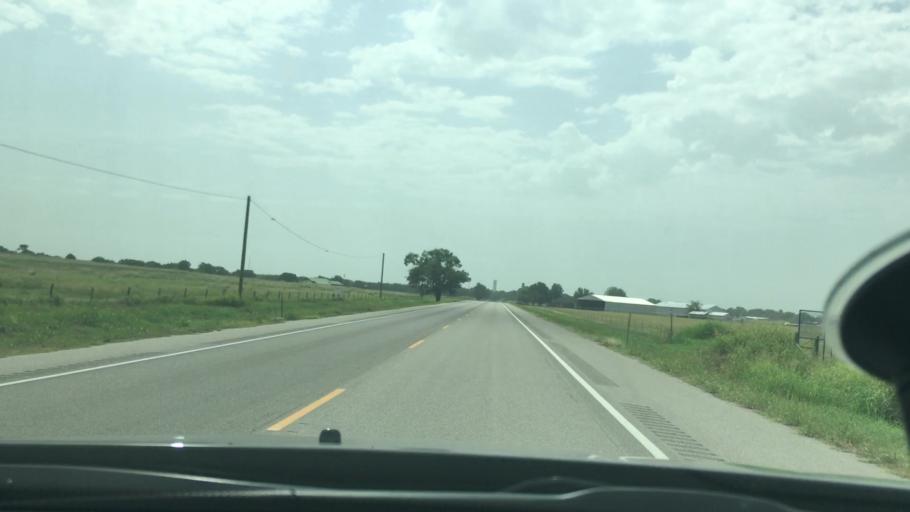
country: US
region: Oklahoma
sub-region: Garvin County
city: Pauls Valley
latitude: 34.8387
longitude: -97.2699
